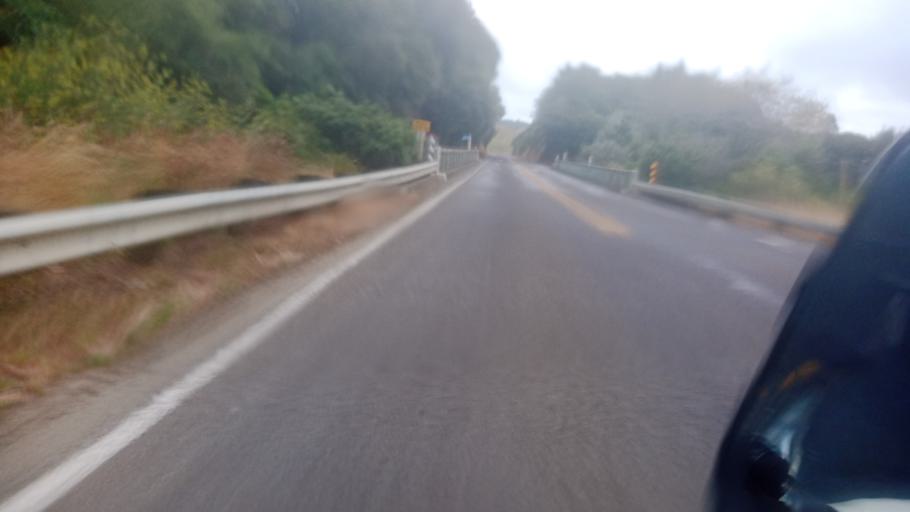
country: NZ
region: Bay of Plenty
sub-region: Opotiki District
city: Opotiki
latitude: -38.4156
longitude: 177.5606
